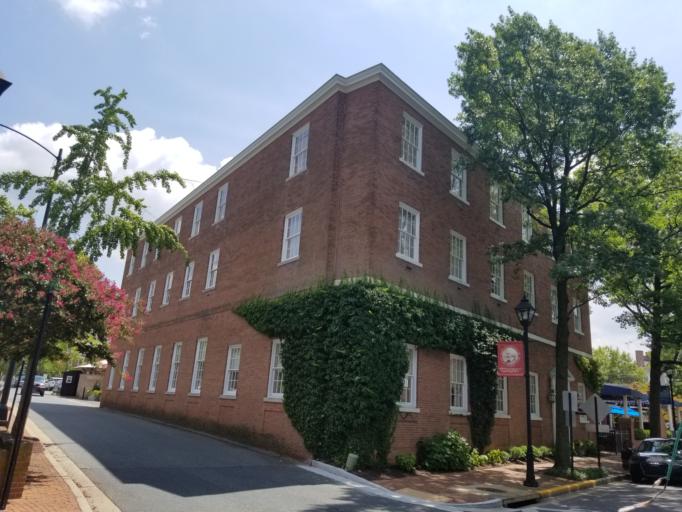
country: US
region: Maryland
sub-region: Talbot County
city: Easton
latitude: 38.7751
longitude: -76.0749
